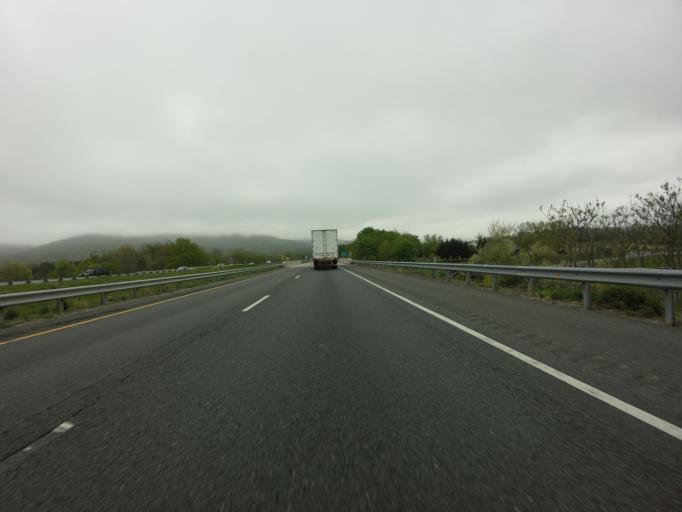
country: US
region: Maryland
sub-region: Washington County
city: Robinwood
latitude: 39.5793
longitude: -77.6298
